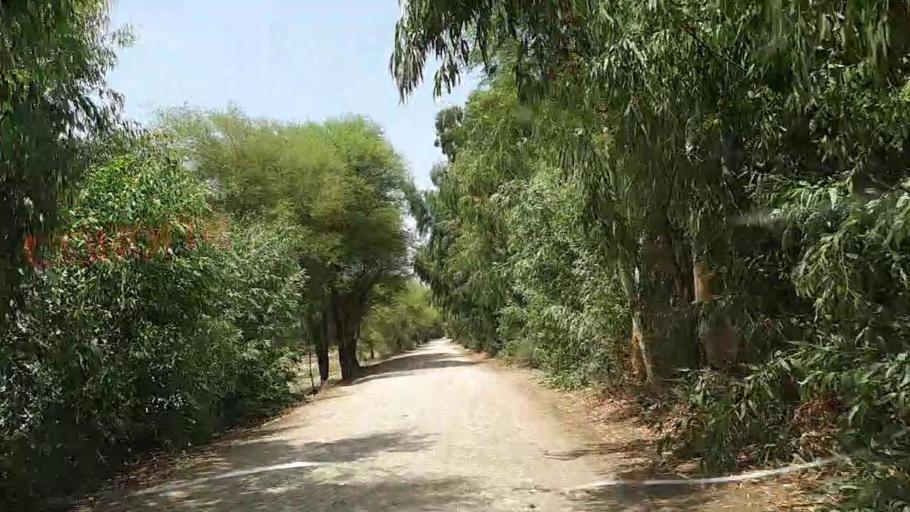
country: PK
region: Sindh
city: Ghotki
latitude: 28.0844
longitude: 69.3115
